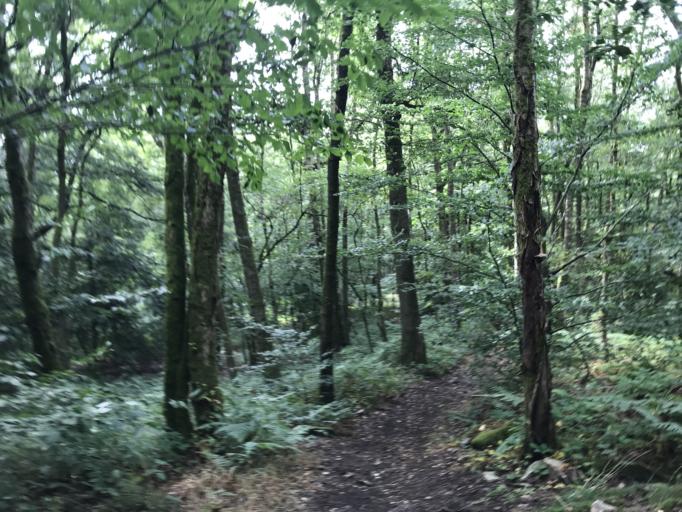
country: FR
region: Champagne-Ardenne
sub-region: Departement des Ardennes
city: Thilay
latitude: 49.8815
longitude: 4.7838
